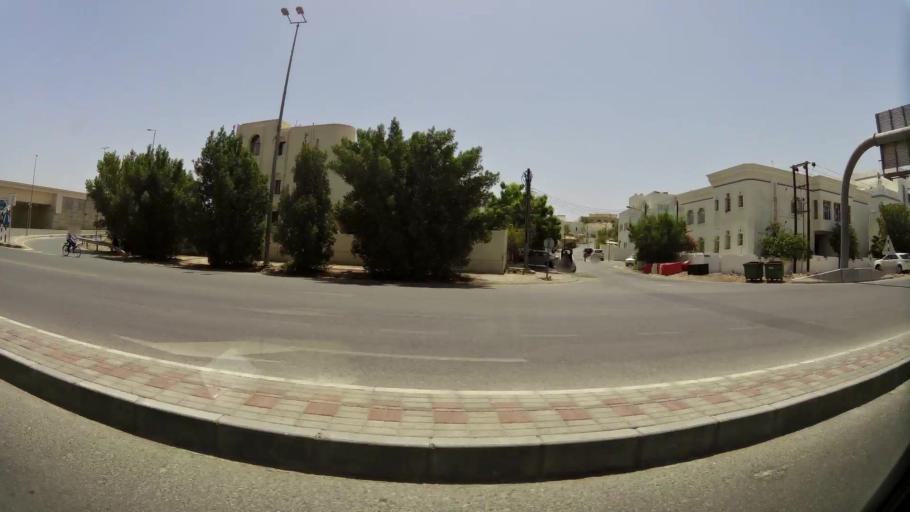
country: OM
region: Muhafazat Masqat
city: Bawshar
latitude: 23.5900
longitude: 58.4475
